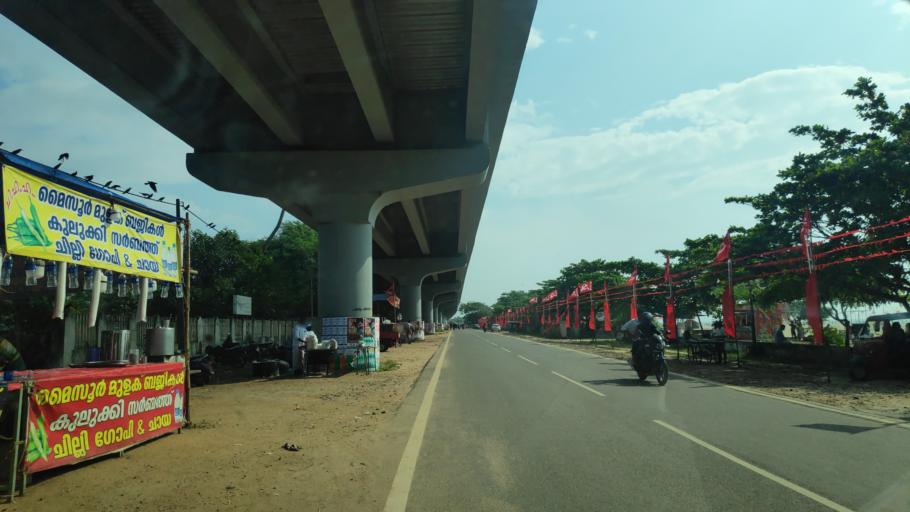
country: IN
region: Kerala
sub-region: Alappuzha
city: Alleppey
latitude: 9.4953
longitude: 76.3182
